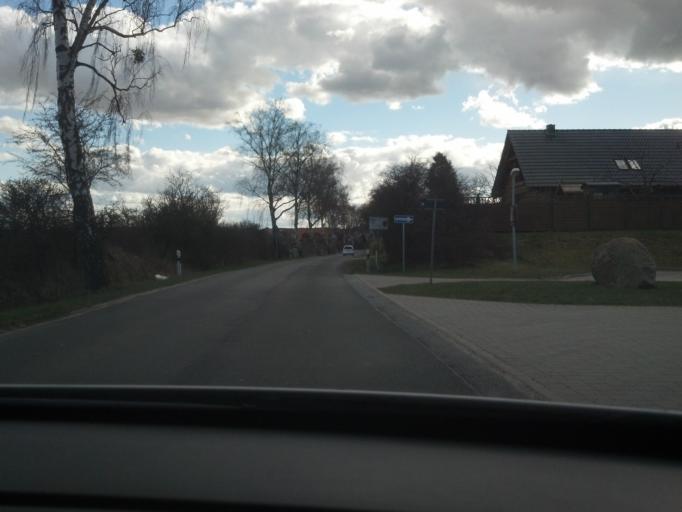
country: DE
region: Mecklenburg-Vorpommern
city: Burg Stargard
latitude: 53.5031
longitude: 13.3229
